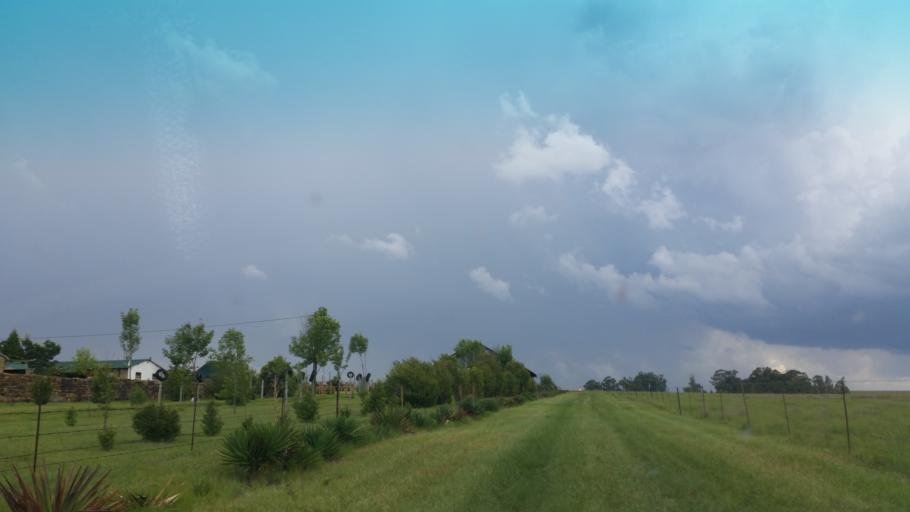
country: ZA
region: Orange Free State
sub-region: Thabo Mofutsanyana District Municipality
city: Harrismith
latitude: -28.1915
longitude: 29.0133
